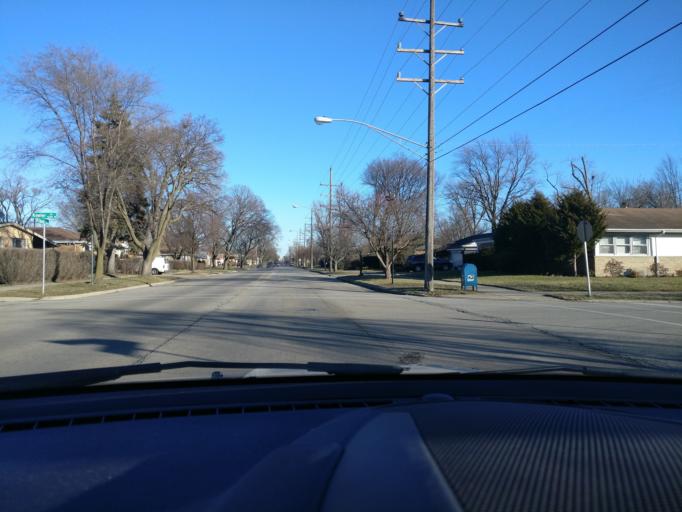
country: US
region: Illinois
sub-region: Cook County
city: Skokie
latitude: 42.0480
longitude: -87.7326
